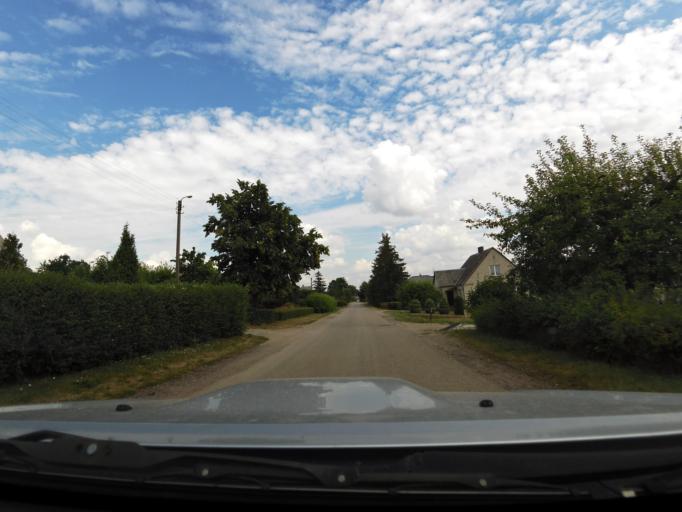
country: LT
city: Gelgaudiskis
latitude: 55.0994
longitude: 22.9758
